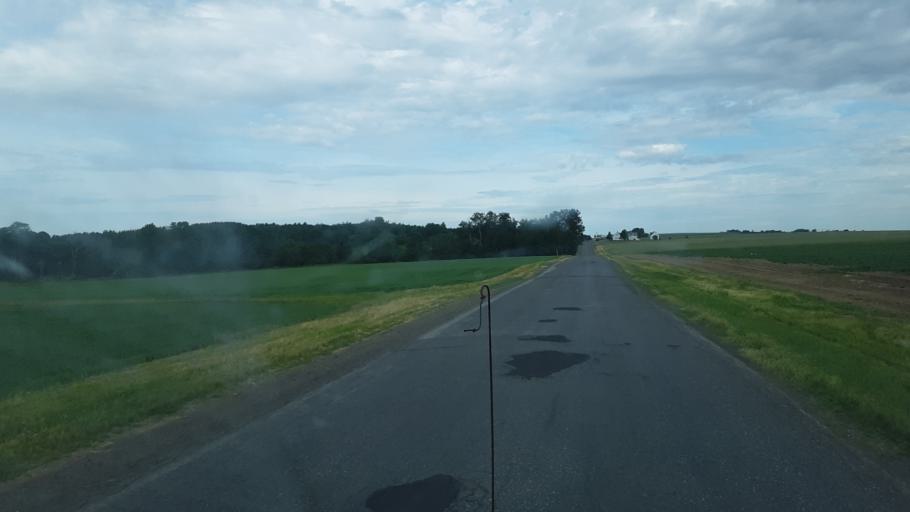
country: US
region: Maine
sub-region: Aroostook County
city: Caribou
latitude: 46.8114
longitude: -68.0048
